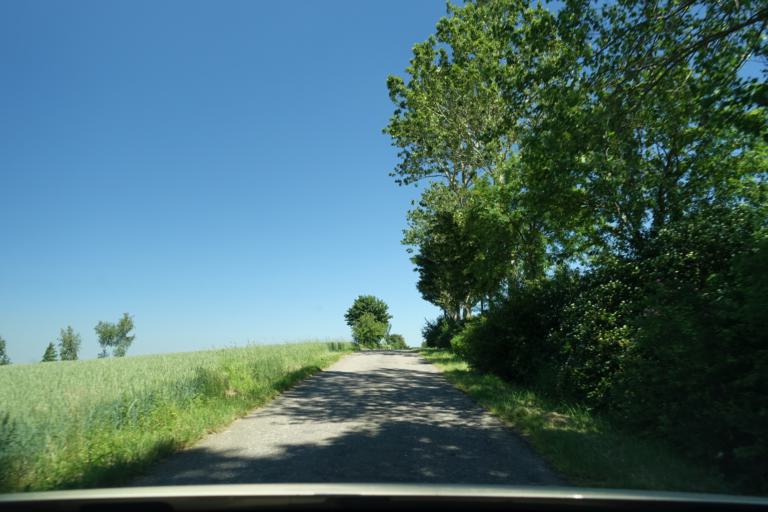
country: DE
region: Saxony
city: Eppendorf
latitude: 50.8205
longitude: 13.2485
